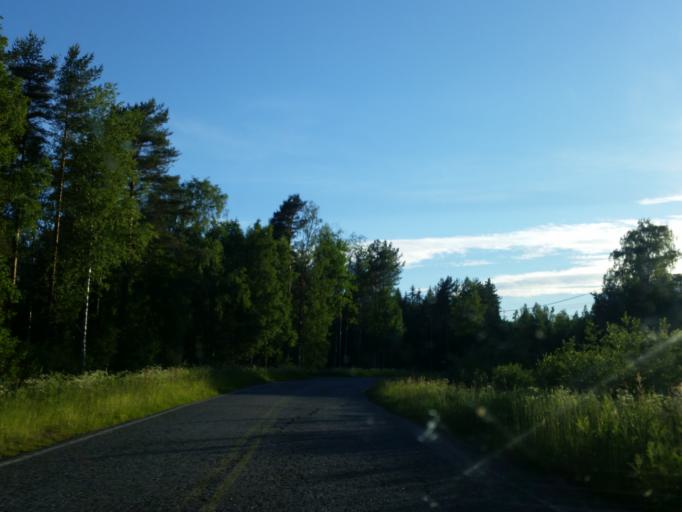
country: FI
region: Northern Savo
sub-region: Sisae-Savo
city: Tervo
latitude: 63.0302
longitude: 26.7050
